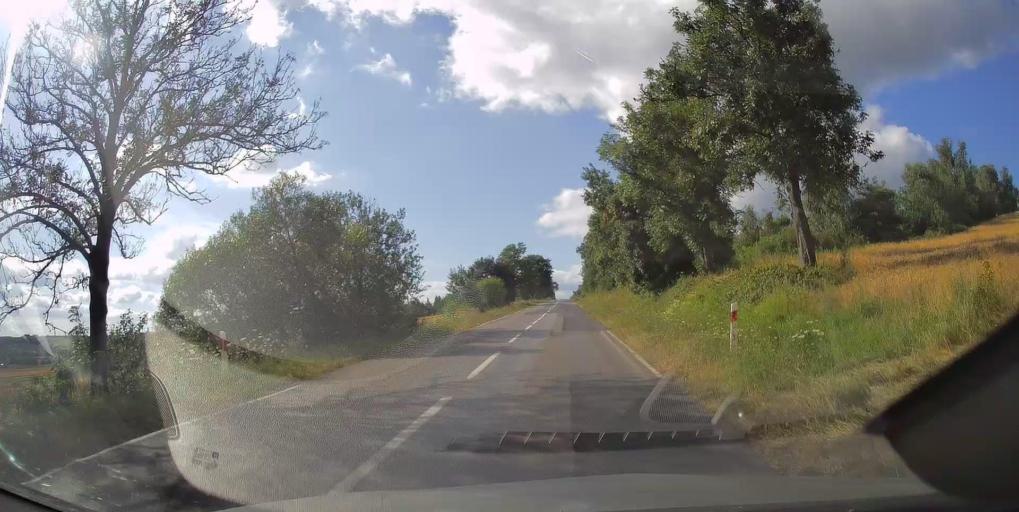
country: PL
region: Swietokrzyskie
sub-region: Powiat skarzyski
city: Suchedniow
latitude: 50.9862
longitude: 20.8685
